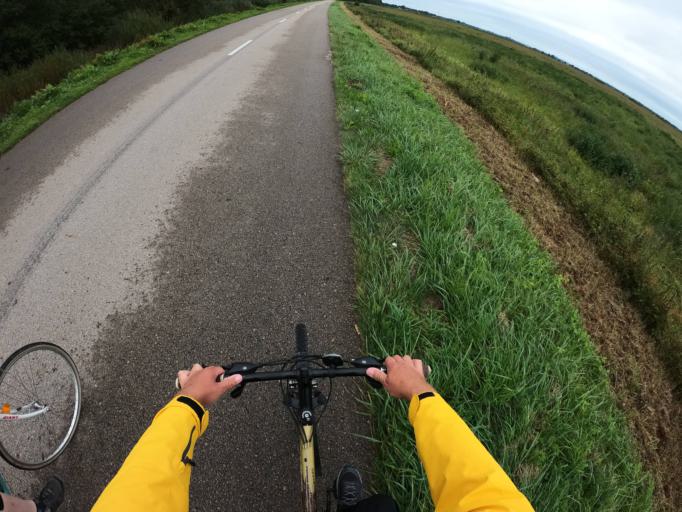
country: LT
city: Rusne
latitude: 55.3401
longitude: 21.3597
